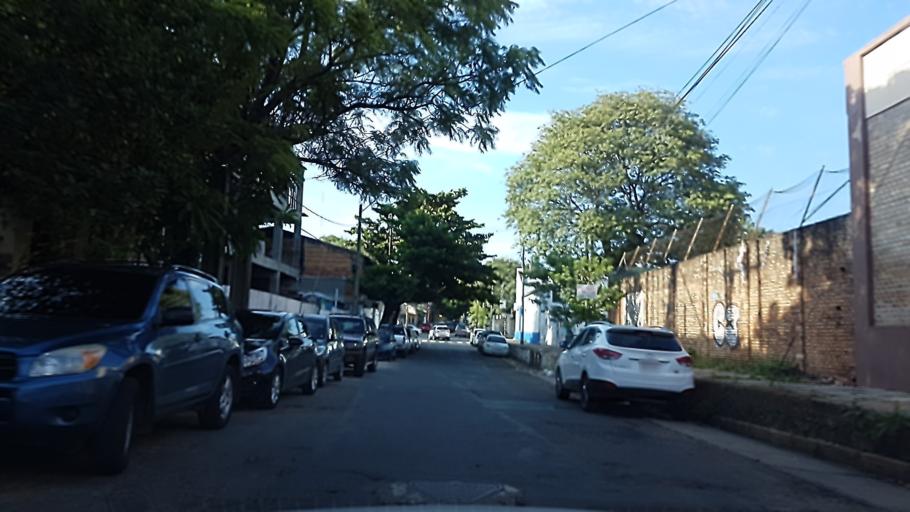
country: PY
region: Asuncion
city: Asuncion
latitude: -25.2872
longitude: -57.6066
